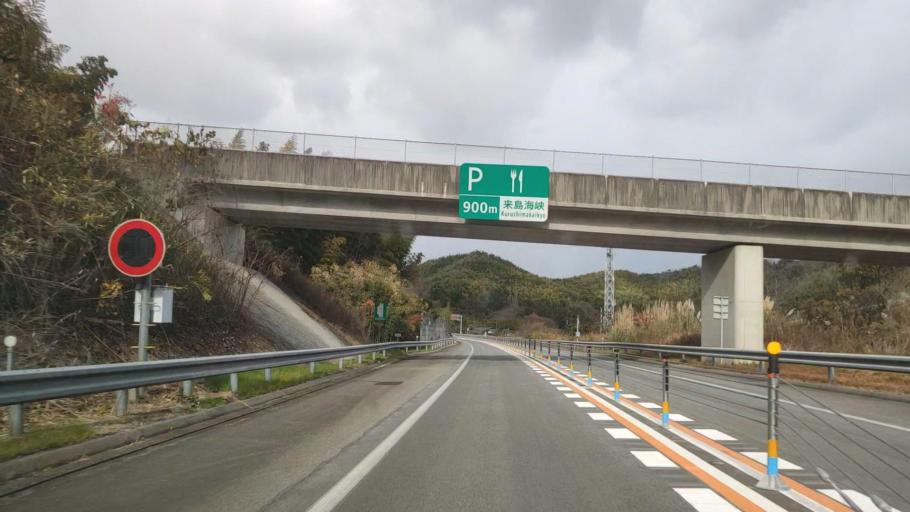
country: JP
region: Ehime
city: Hojo
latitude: 34.0885
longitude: 132.9787
